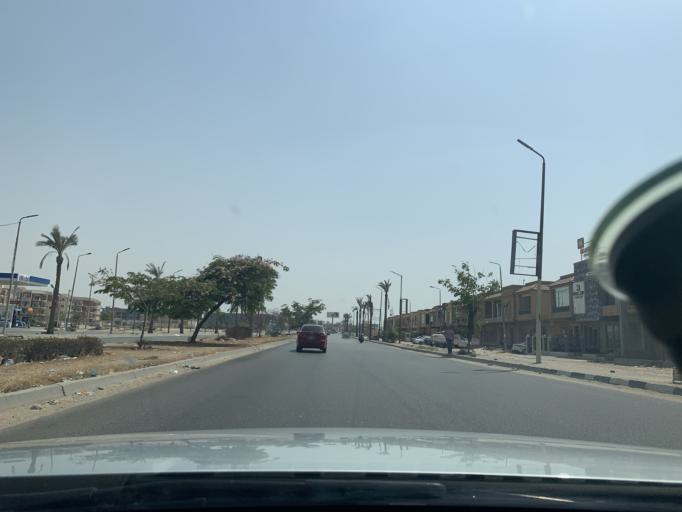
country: EG
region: Muhafazat al Qalyubiyah
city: Al Khankah
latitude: 30.0897
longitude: 31.3689
